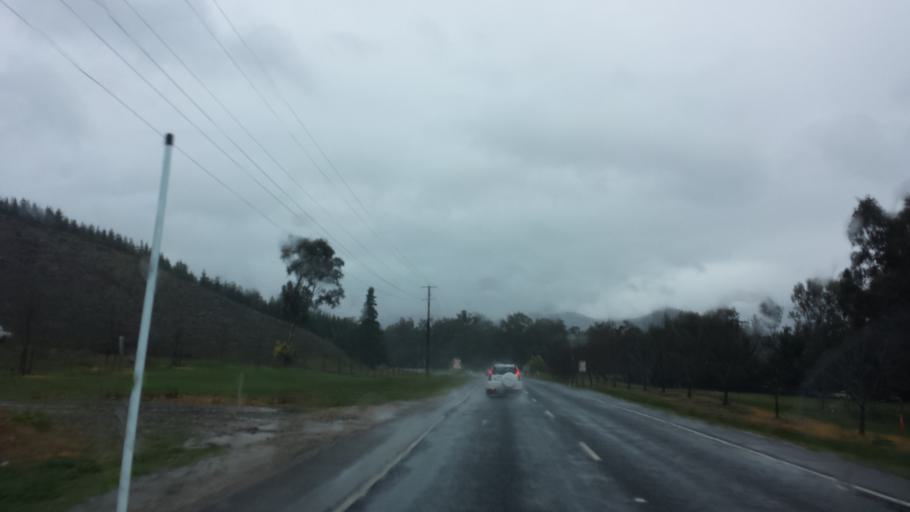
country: AU
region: Victoria
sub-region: Alpine
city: Mount Beauty
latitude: -36.5784
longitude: 146.7497
